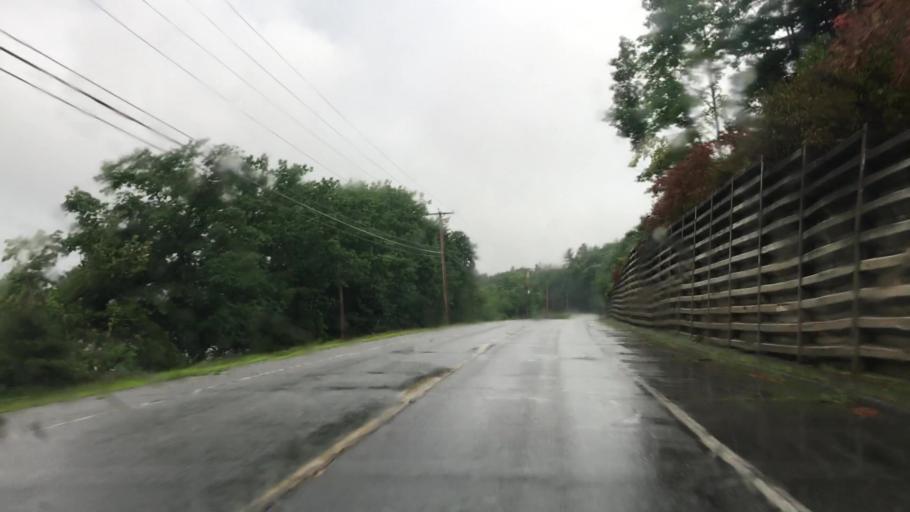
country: US
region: Maine
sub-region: Kennebec County
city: Pittston
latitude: 44.2097
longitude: -69.7639
